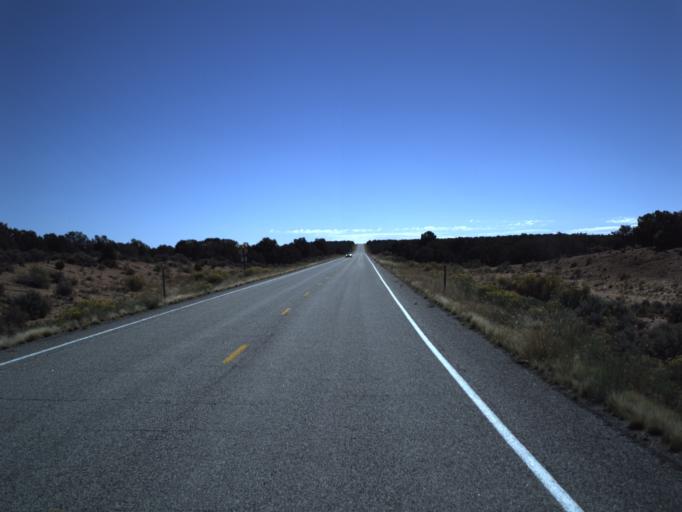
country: US
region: Utah
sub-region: San Juan County
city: Blanding
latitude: 37.5563
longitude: -109.9999
